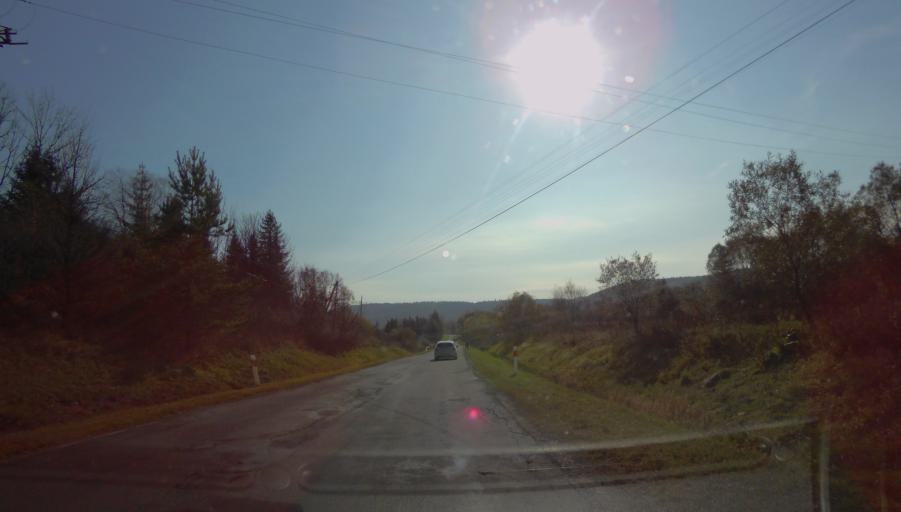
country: PL
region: Subcarpathian Voivodeship
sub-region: Powiat sanocki
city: Komancza
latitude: 49.2387
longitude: 22.1454
